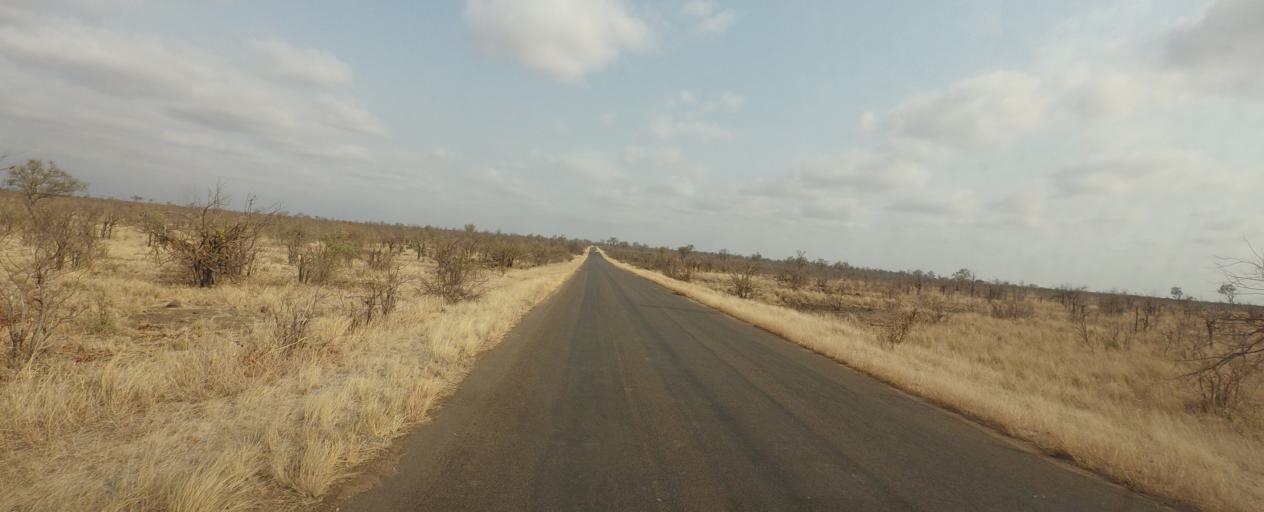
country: ZA
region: Limpopo
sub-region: Vhembe District Municipality
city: Mutale
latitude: -22.8950
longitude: 31.2500
